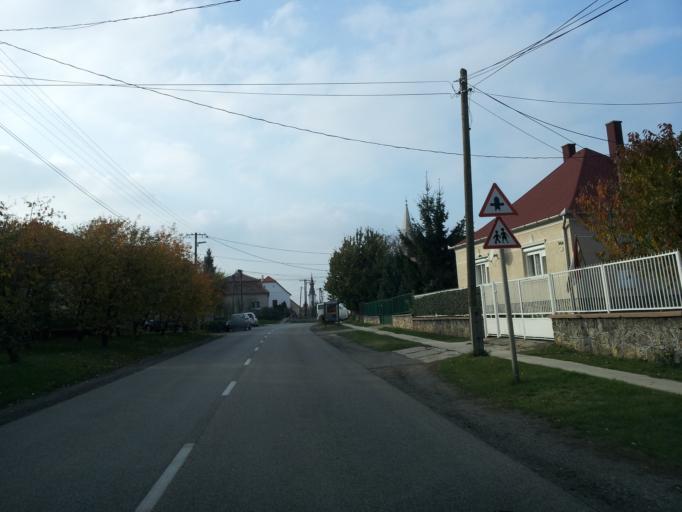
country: HU
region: Komarom-Esztergom
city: Bokod
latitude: 47.4911
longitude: 18.2501
